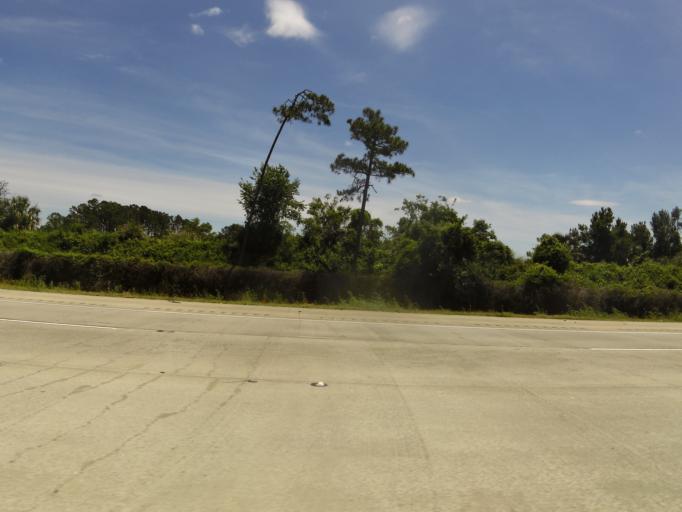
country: US
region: Georgia
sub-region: Glynn County
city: Country Club Estates
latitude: 31.2688
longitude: -81.4922
